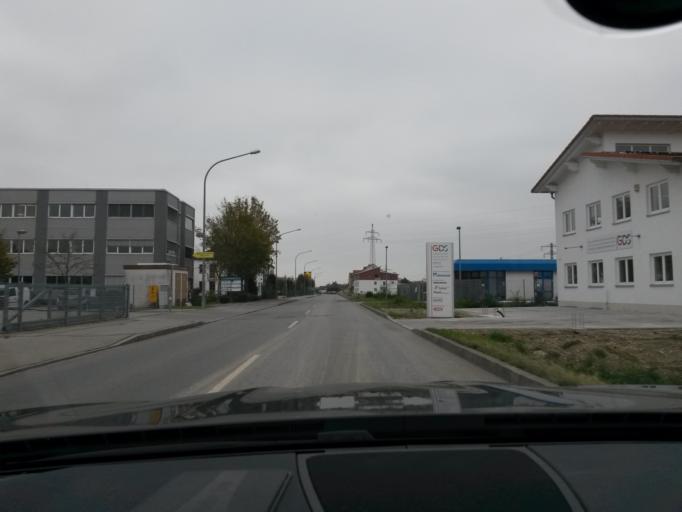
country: DE
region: Bavaria
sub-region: Lower Bavaria
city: Tiefenbach
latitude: 48.5446
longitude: 12.0921
